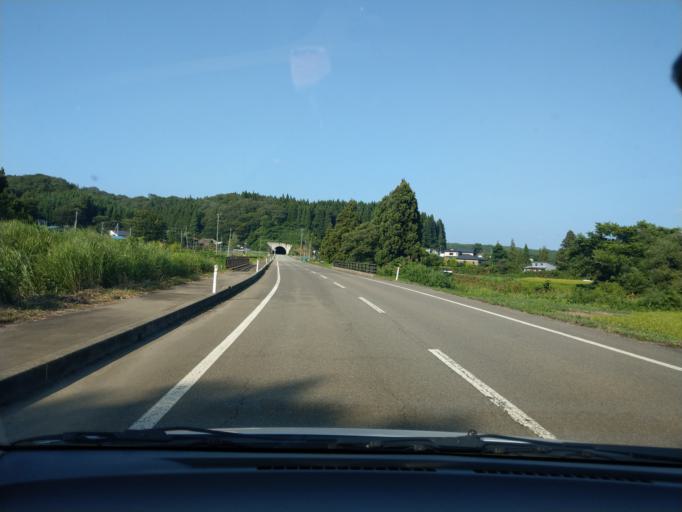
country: JP
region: Akita
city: Akita
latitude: 39.6002
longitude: 140.2158
